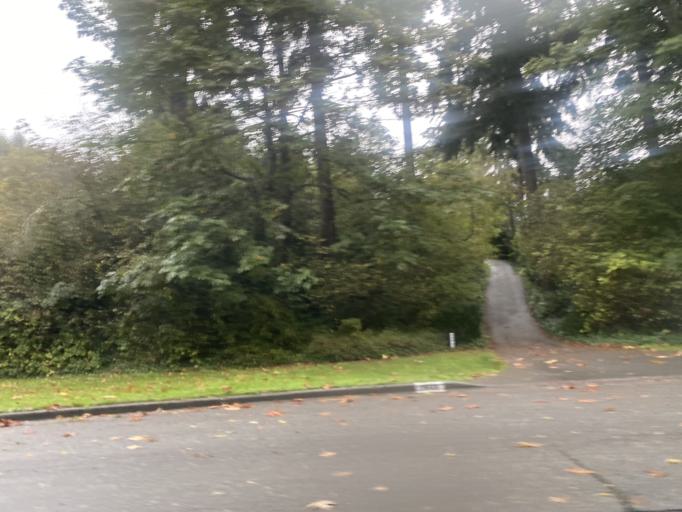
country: US
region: Washington
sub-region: King County
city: Seattle
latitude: 47.6443
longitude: -122.4129
